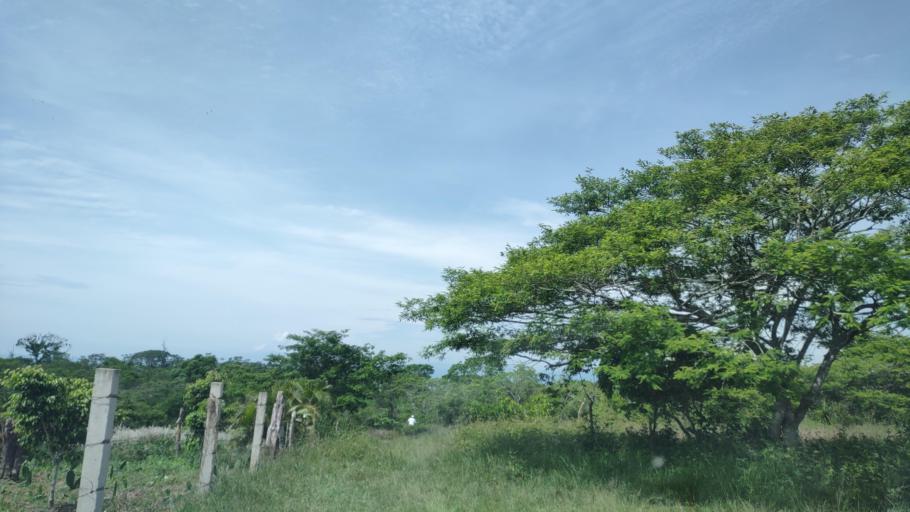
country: MX
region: Veracruz
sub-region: Emiliano Zapata
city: Jacarandas
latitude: 19.4723
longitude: -96.8314
